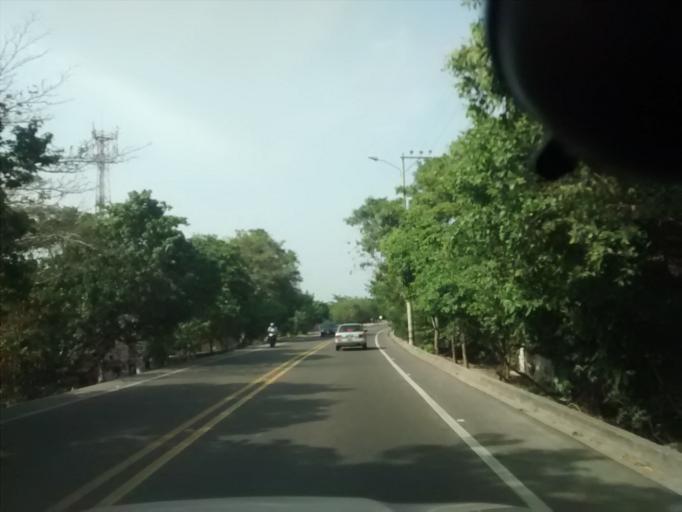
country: CO
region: Bolivar
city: Cartagena
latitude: 10.4744
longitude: -75.4938
